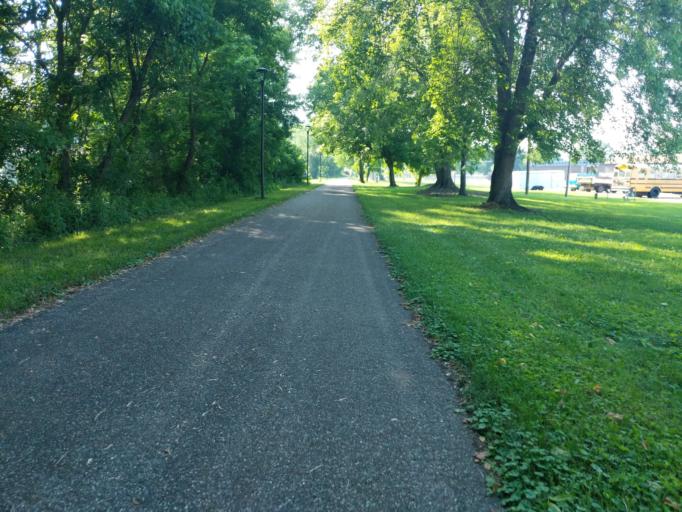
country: US
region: Ohio
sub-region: Athens County
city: Nelsonville
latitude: 39.4316
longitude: -82.2098
